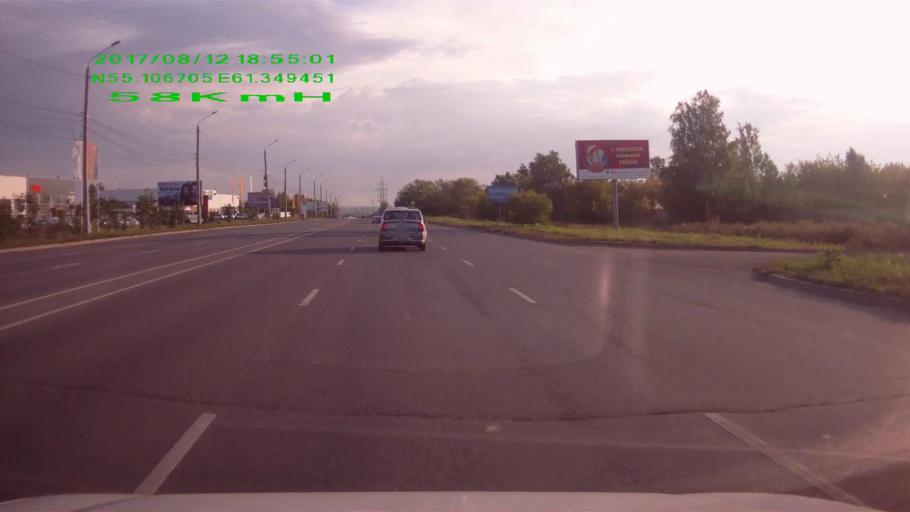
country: RU
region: Chelyabinsk
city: Novosineglazovskiy
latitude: 55.1015
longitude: 61.3418
